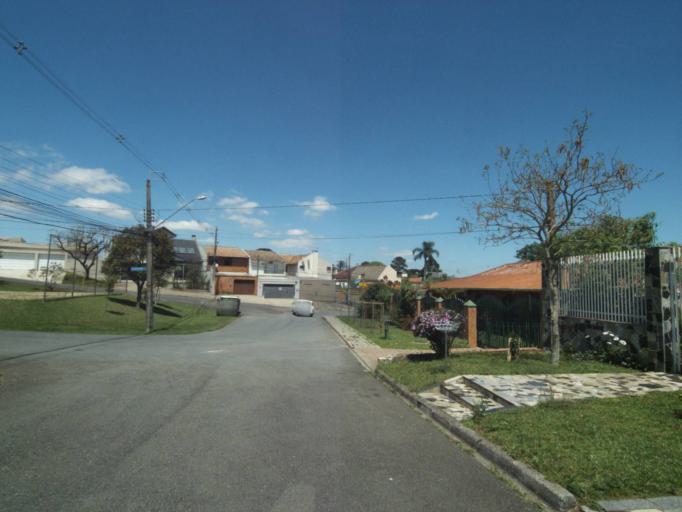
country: BR
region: Parana
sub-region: Curitiba
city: Curitiba
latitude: -25.3941
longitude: -49.2641
